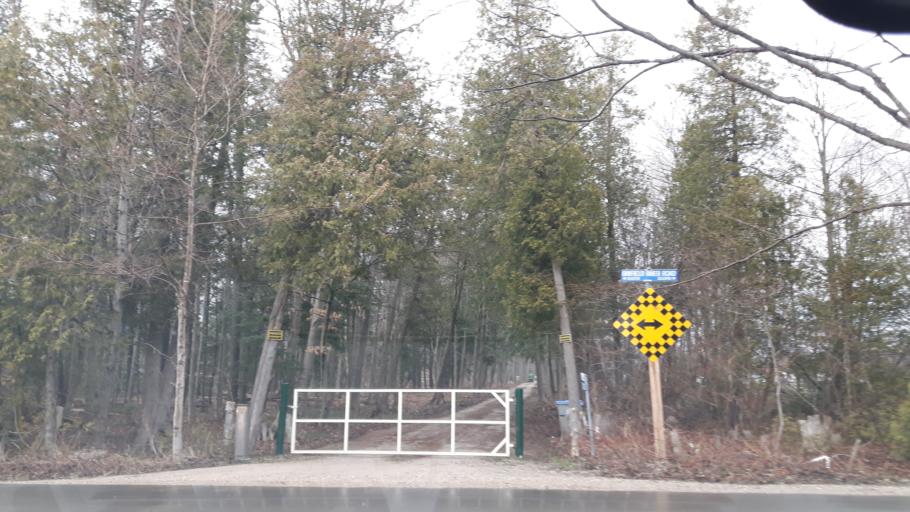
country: CA
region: Ontario
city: Bluewater
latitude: 43.5756
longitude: -81.6925
